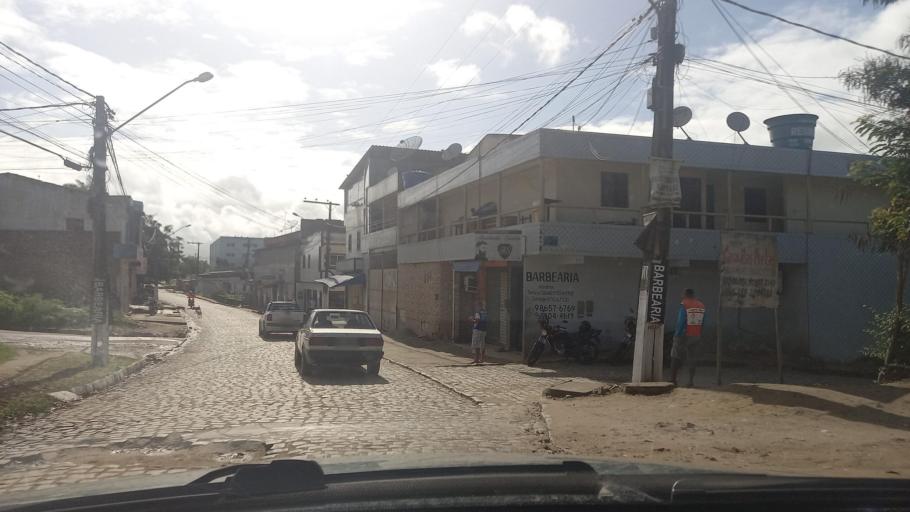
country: BR
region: Pernambuco
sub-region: Vitoria De Santo Antao
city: Vitoria de Santo Antao
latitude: -8.0990
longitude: -35.2794
